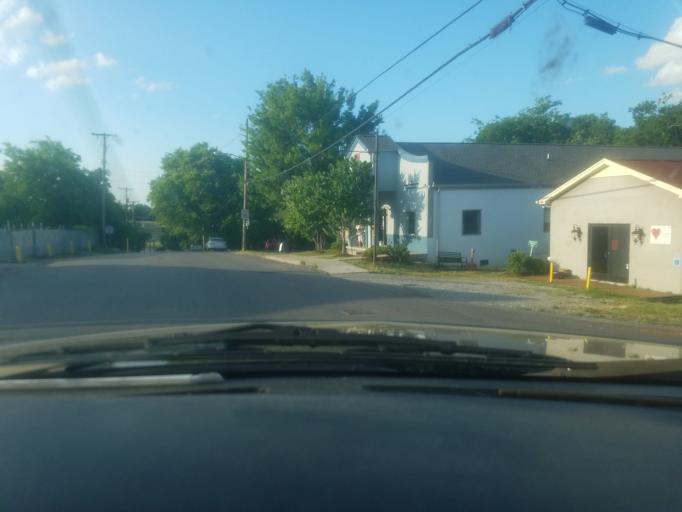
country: US
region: Tennessee
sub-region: Davidson County
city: Nashville
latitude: 36.1611
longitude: -86.8403
